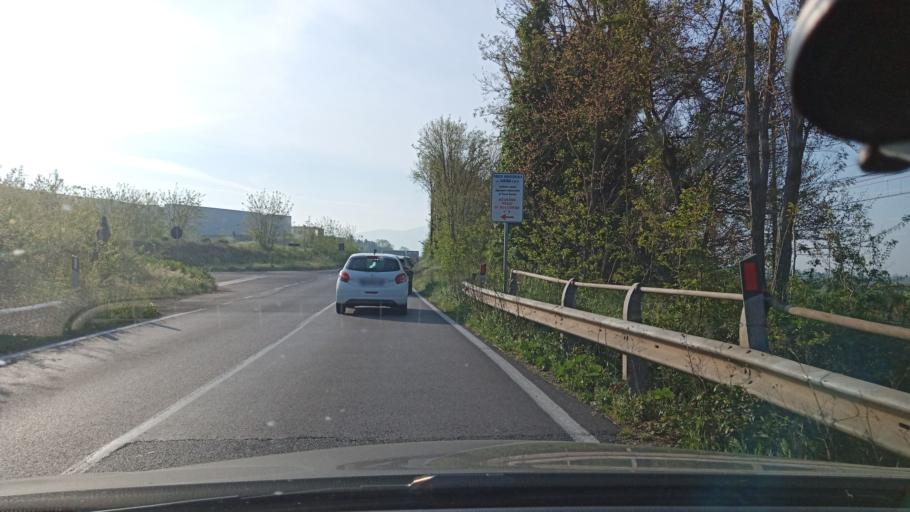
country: IT
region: Latium
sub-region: Citta metropolitana di Roma Capitale
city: Fiano Romano
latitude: 42.1686
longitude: 12.6381
